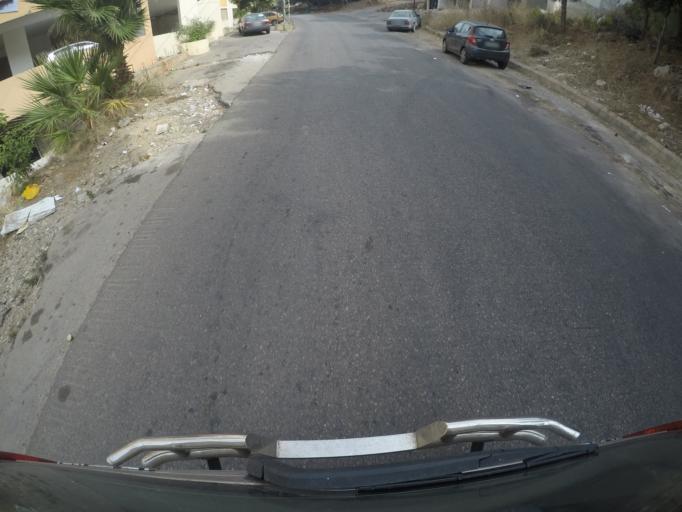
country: LB
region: Mont-Liban
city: Beit ed Dine
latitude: 33.7364
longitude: 35.4909
